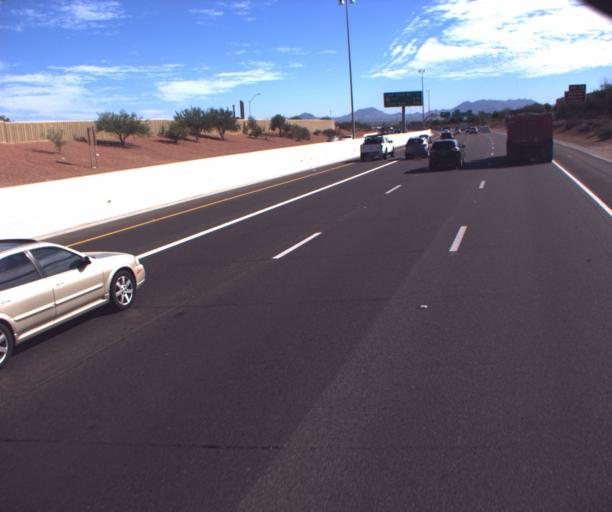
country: US
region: Arizona
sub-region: Maricopa County
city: Paradise Valley
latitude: 33.6688
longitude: -112.0440
